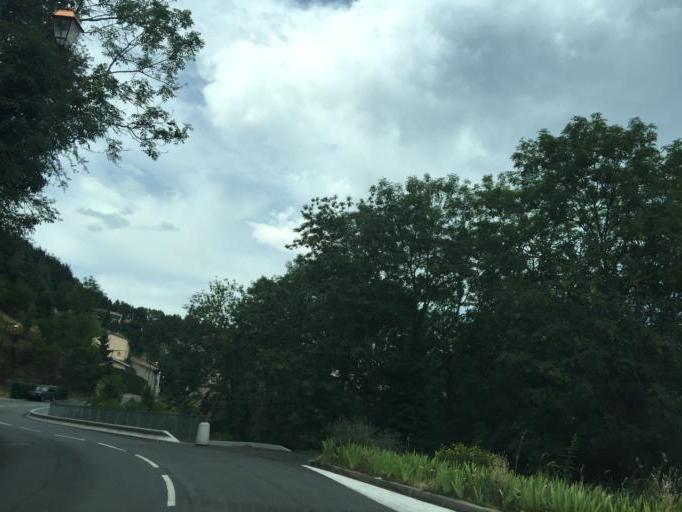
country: FR
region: Rhone-Alpes
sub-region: Departement de la Loire
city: Saint-Jean-Bonnefonds
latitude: 45.4106
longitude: 4.4396
